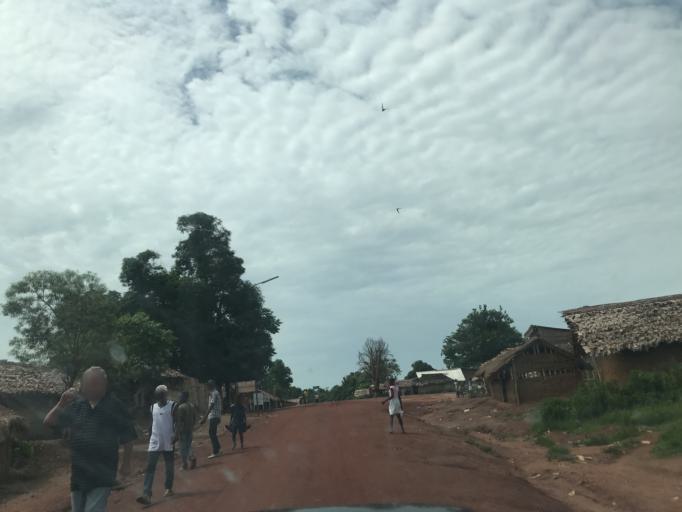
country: CD
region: Eastern Province
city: Buta
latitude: 2.7854
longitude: 24.7314
